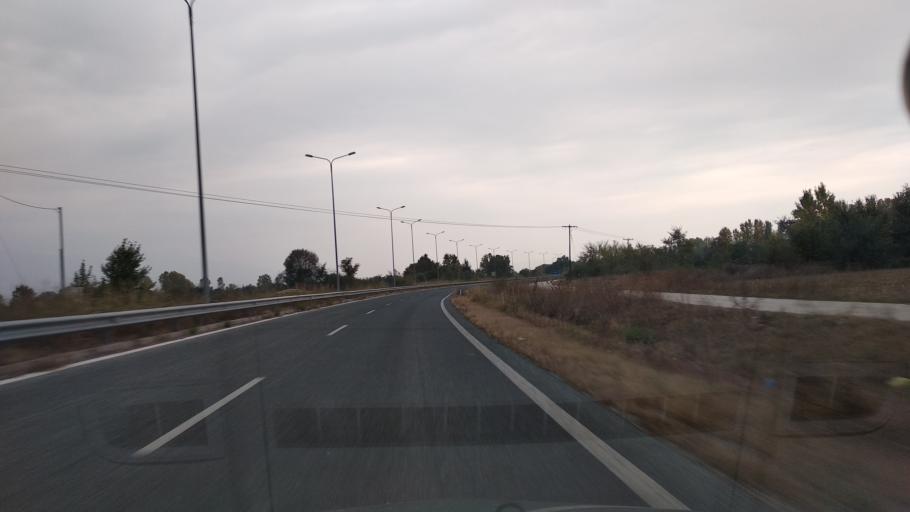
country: GR
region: Thessaly
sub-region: Trikala
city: Pyrgetos
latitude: 39.5366
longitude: 21.7371
